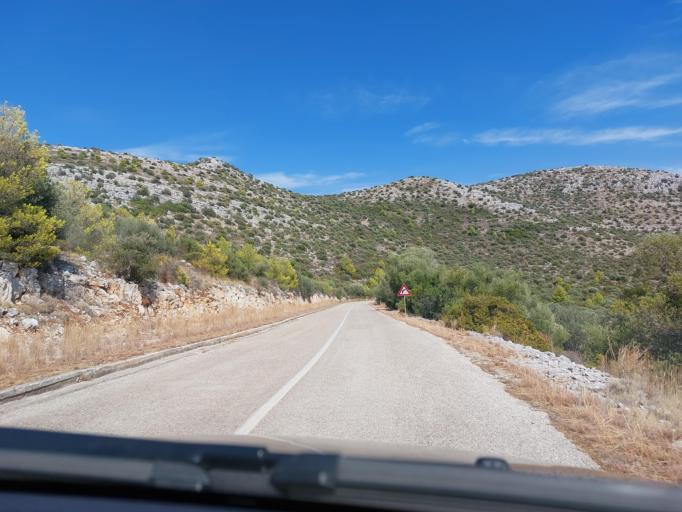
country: HR
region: Dubrovacko-Neretvanska
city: Smokvica
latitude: 42.7435
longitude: 16.8805
